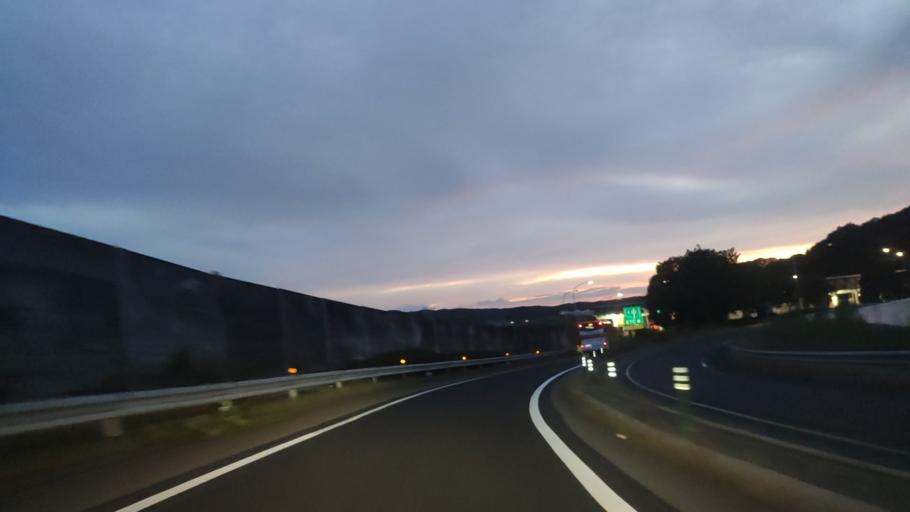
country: JP
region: Hyogo
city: Sandacho
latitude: 34.8876
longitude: 135.1175
